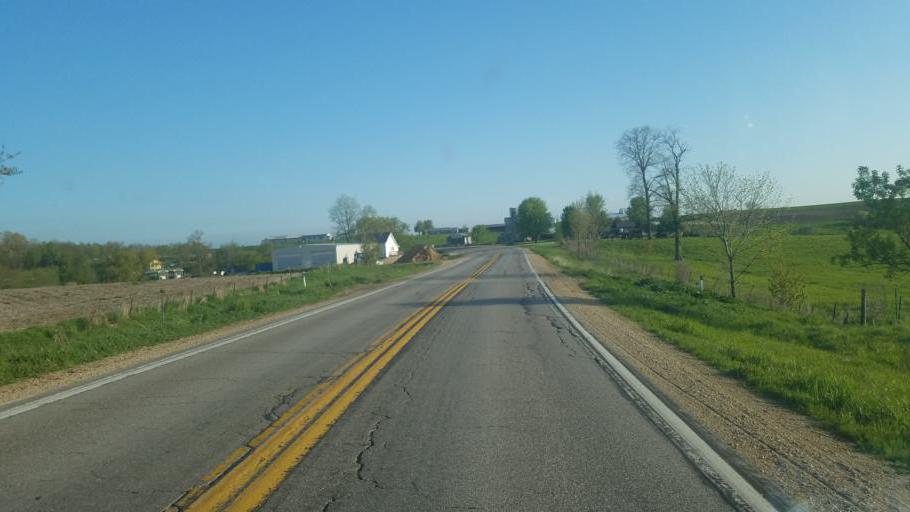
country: US
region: Wisconsin
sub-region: Vernon County
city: Hillsboro
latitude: 43.5950
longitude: -90.4973
